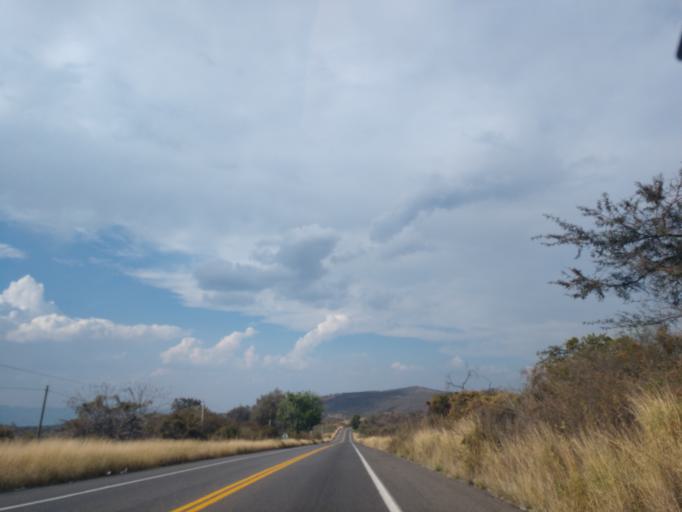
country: MX
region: Jalisco
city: La Manzanilla de la Paz
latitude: 20.0740
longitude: -103.1707
